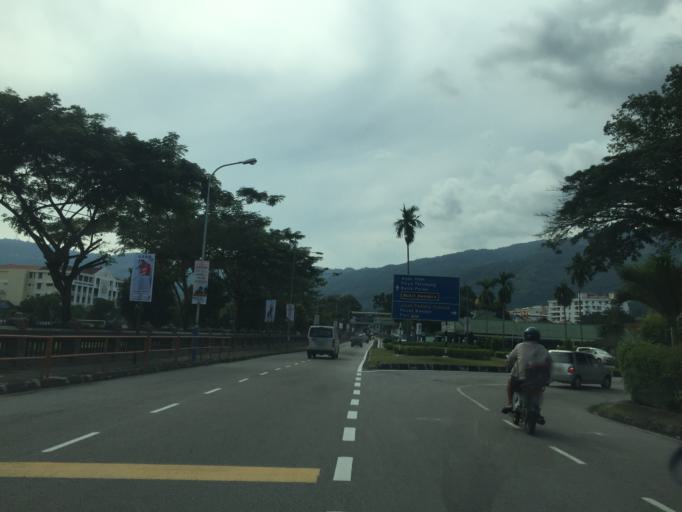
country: MY
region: Penang
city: George Town
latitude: 5.4054
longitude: 100.2960
